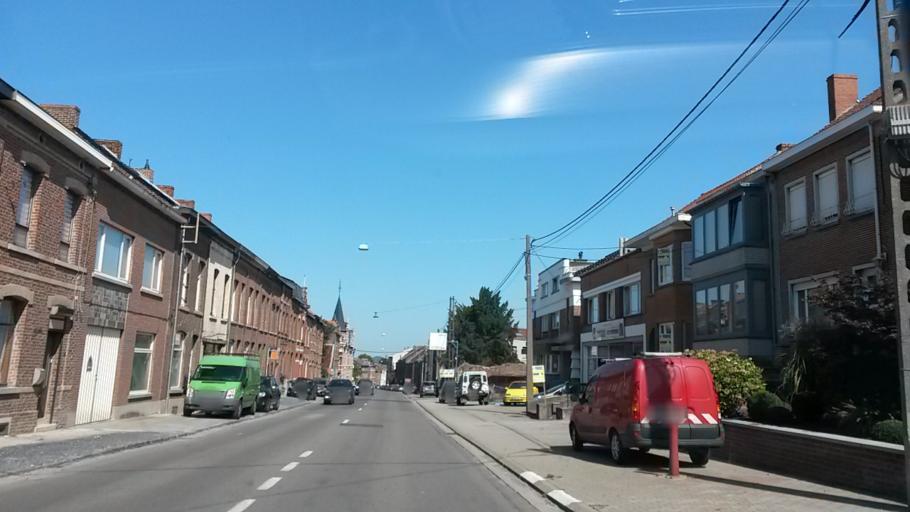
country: BE
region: Wallonia
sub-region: Province du Hainaut
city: Binche
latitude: 50.4042
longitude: 4.1712
